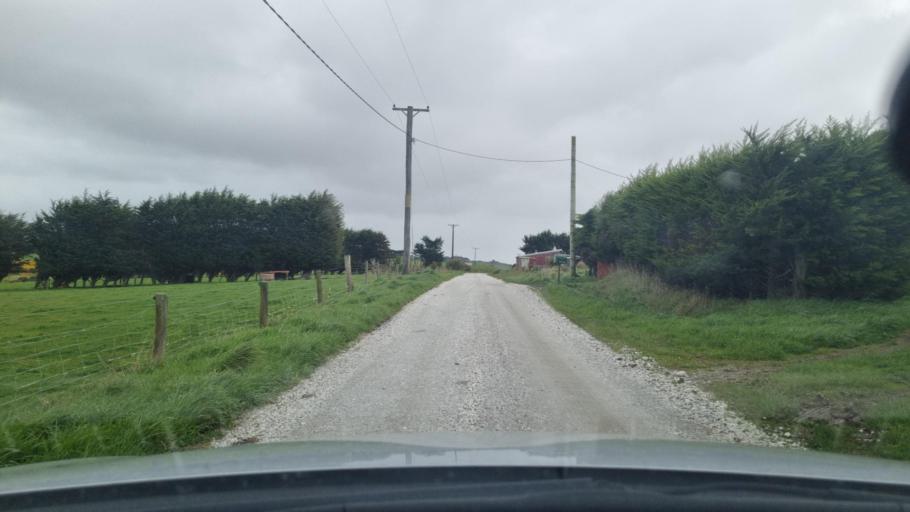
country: NZ
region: Southland
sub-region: Invercargill City
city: Bluff
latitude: -46.5417
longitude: 168.2927
